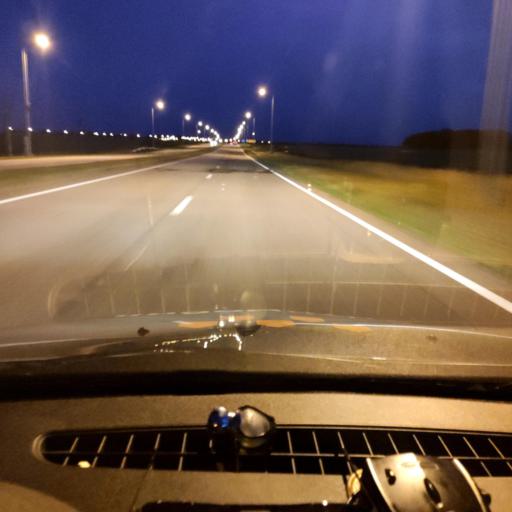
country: RU
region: Belgorod
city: Skorodnoye
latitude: 51.0697
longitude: 37.2045
